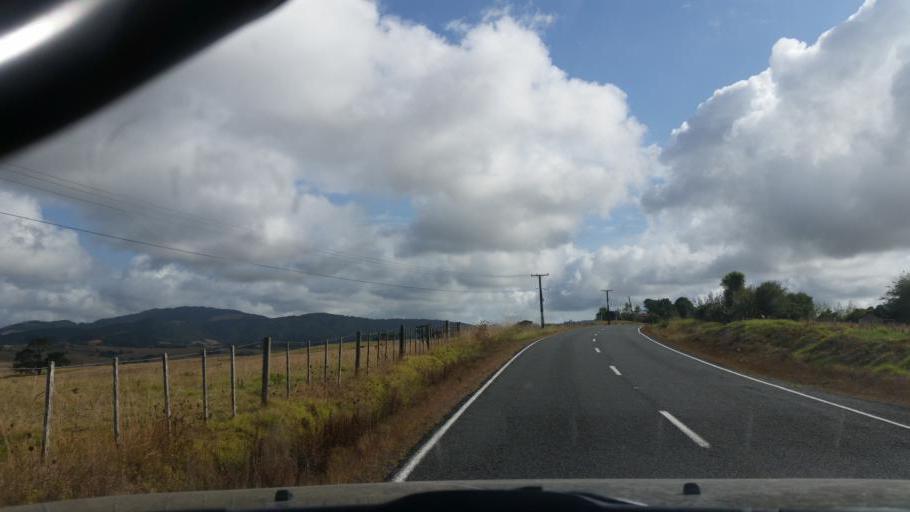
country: NZ
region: Auckland
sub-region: Auckland
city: Wellsford
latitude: -36.1490
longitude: 174.4756
